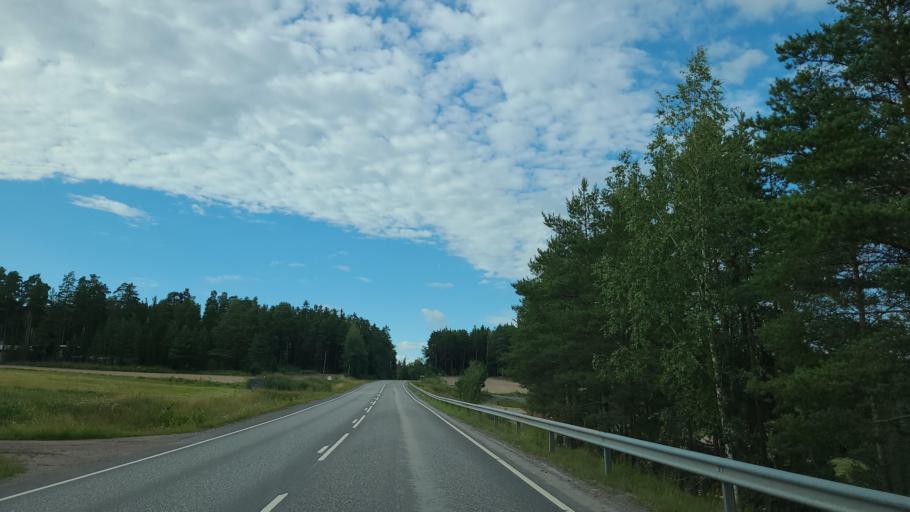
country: FI
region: Varsinais-Suomi
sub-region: Turku
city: Merimasku
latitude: 60.4339
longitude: 21.8956
